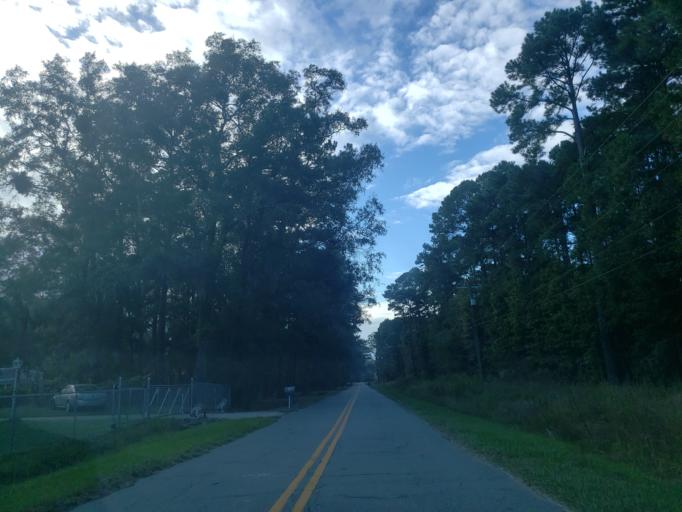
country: US
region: Georgia
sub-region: Chatham County
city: Georgetown
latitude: 31.9946
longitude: -81.2392
